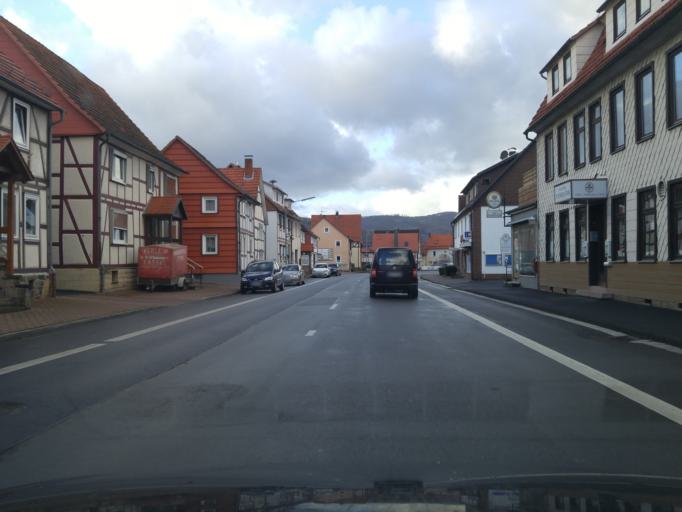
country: DE
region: Lower Saxony
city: Buhren
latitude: 51.4792
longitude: 9.6181
